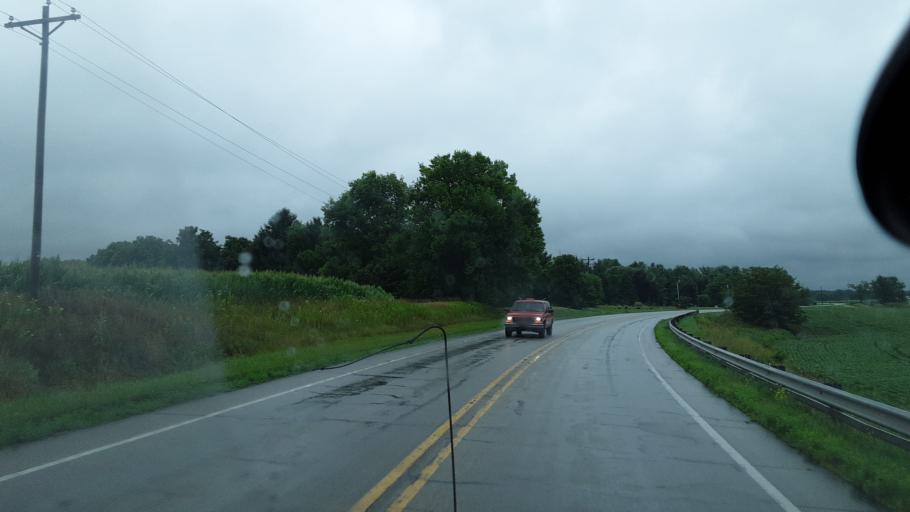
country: US
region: Indiana
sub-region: Adams County
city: Decatur
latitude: 40.7621
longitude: -84.8107
